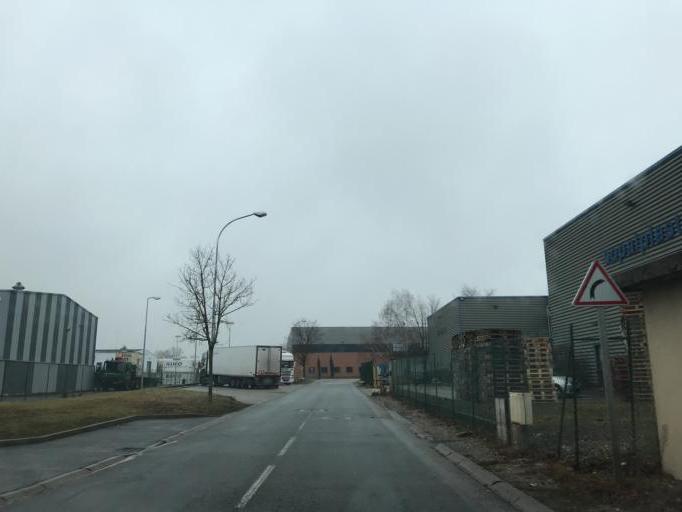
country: FR
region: Rhone-Alpes
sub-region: Departement de l'Ain
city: Mionnay
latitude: 45.8652
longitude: 4.9144
